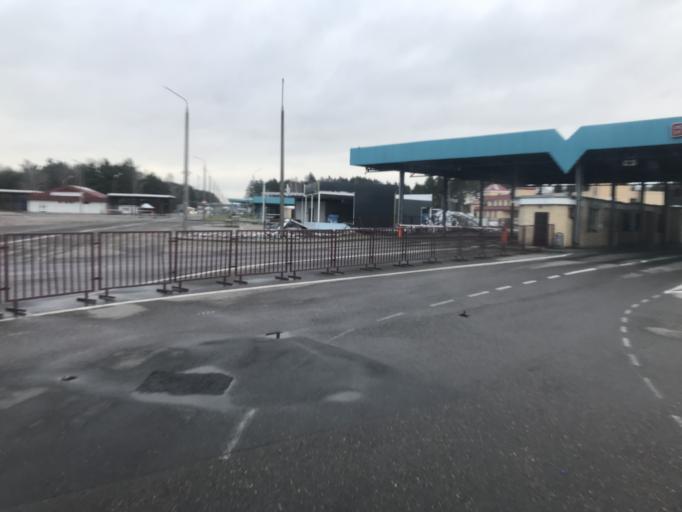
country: BY
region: Grodnenskaya
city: Vyalikaya Byerastavitsa
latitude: 53.1230
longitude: 23.8961
